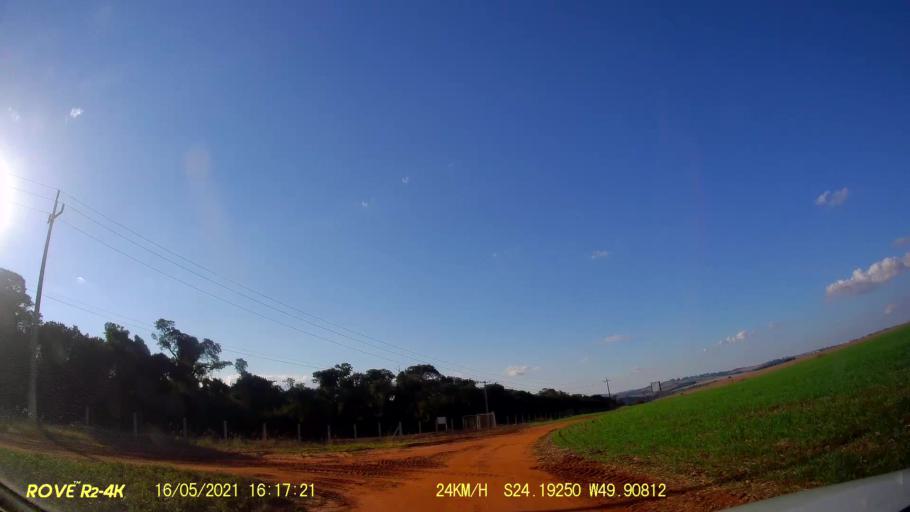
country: BR
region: Parana
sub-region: Jaguariaiva
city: Jaguariaiva
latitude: -24.1925
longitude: -49.9081
